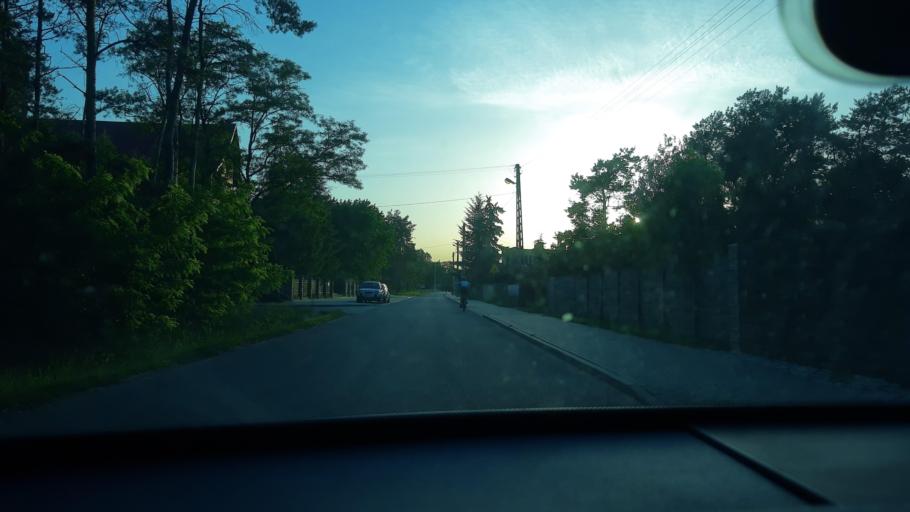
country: PL
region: Lodz Voivodeship
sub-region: Powiat zdunskowolski
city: Zdunska Wola
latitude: 51.6081
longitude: 18.9797
